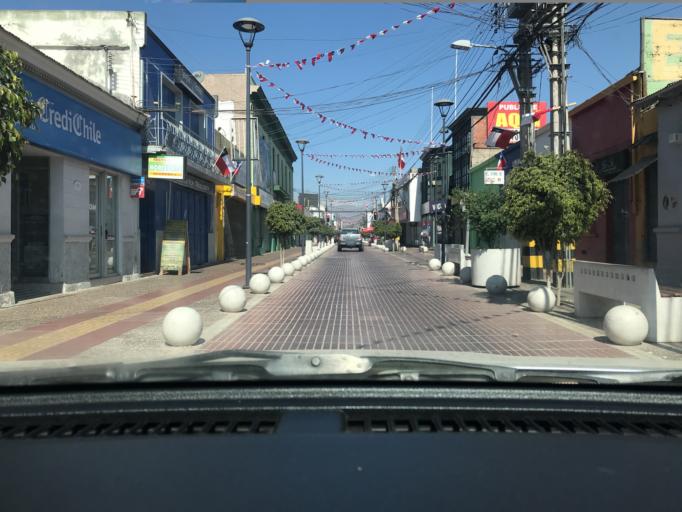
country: CL
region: Atacama
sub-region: Provincia de Huasco
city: Vallenar
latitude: -28.5760
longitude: -70.7599
